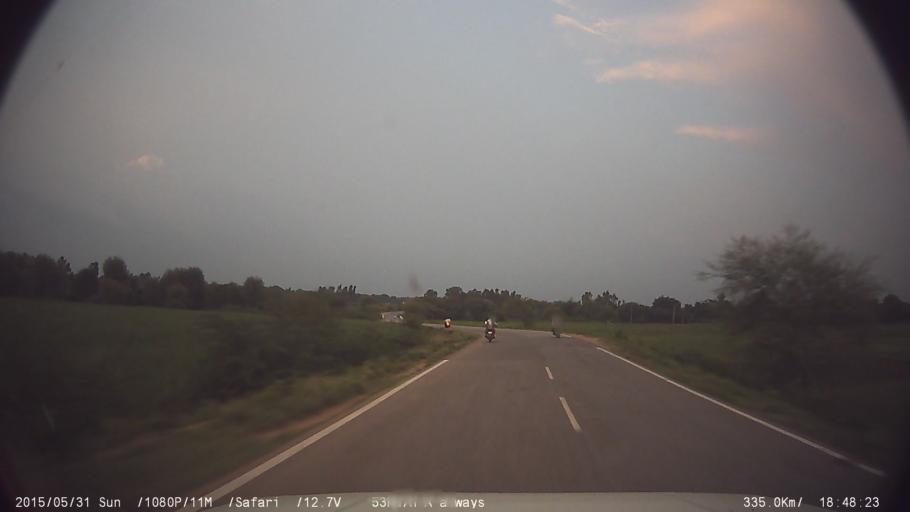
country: IN
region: Karnataka
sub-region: Mysore
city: Tirumakudal Narsipur
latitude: 12.1698
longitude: 76.8423
